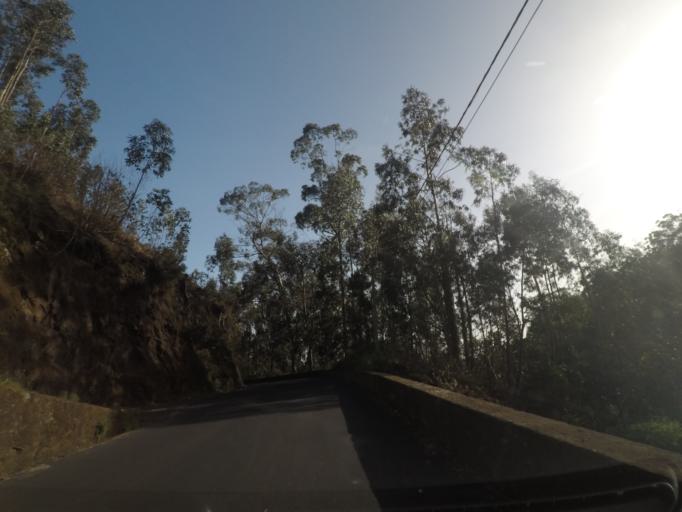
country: PT
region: Madeira
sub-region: Ribeira Brava
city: Campanario
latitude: 32.6740
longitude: -17.0044
